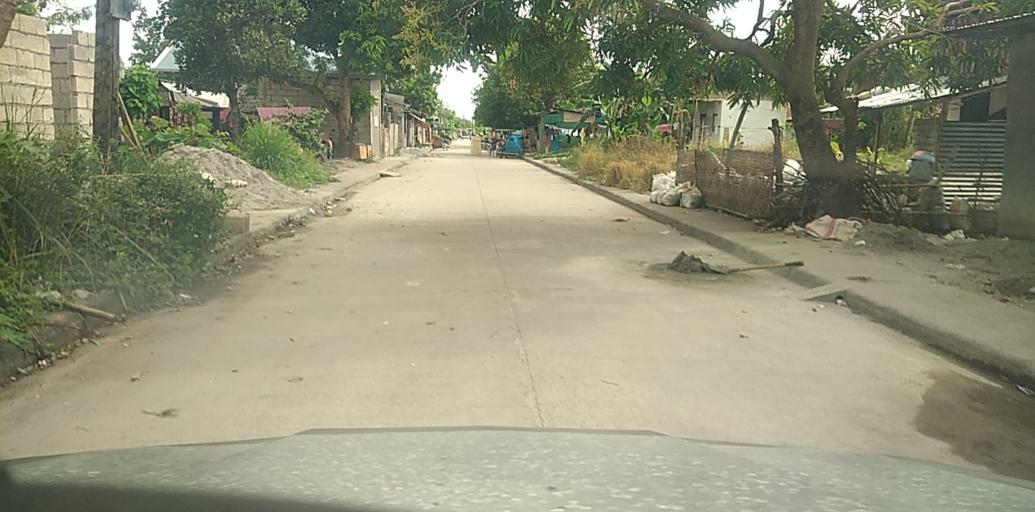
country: PH
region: Central Luzon
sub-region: Province of Pampanga
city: Buensuseso
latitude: 15.1815
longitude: 120.6678
